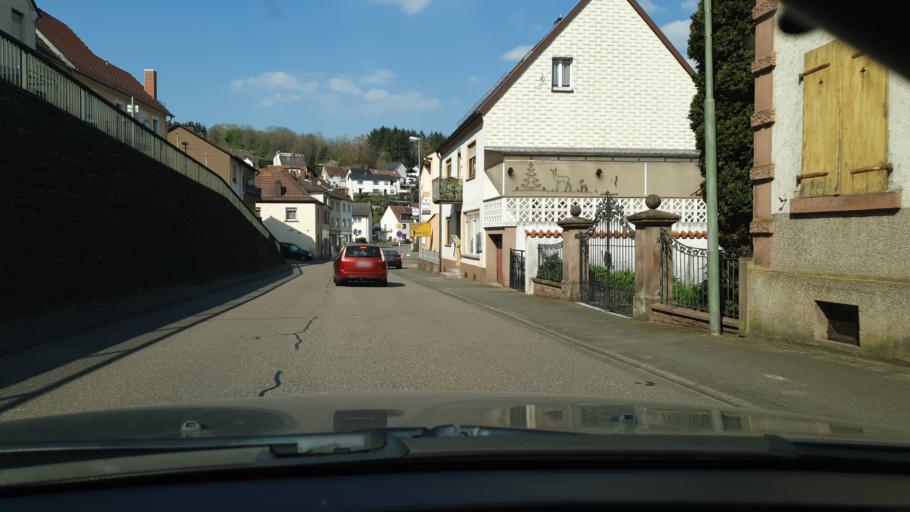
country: DE
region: Rheinland-Pfalz
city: Grossbundenbach
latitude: 49.2758
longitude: 7.4211
